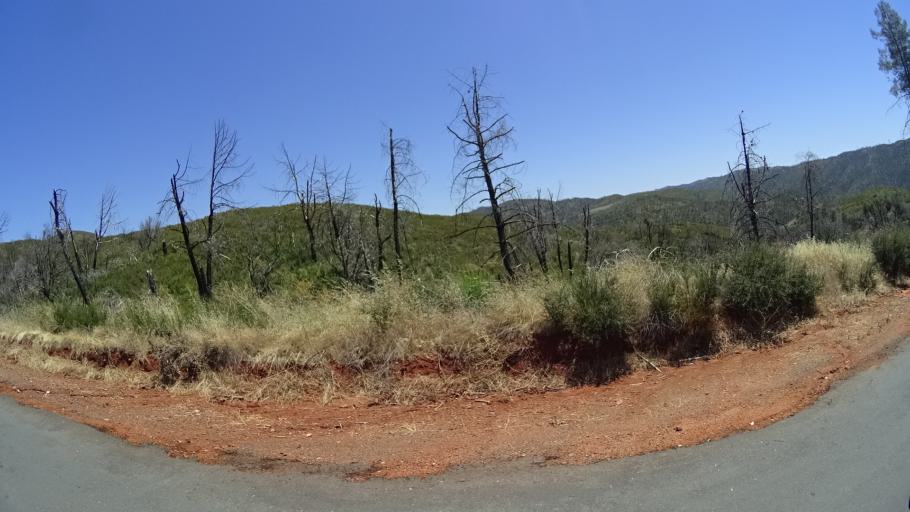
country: US
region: California
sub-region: Calaveras County
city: Mountain Ranch
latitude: 38.2899
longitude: -120.6222
